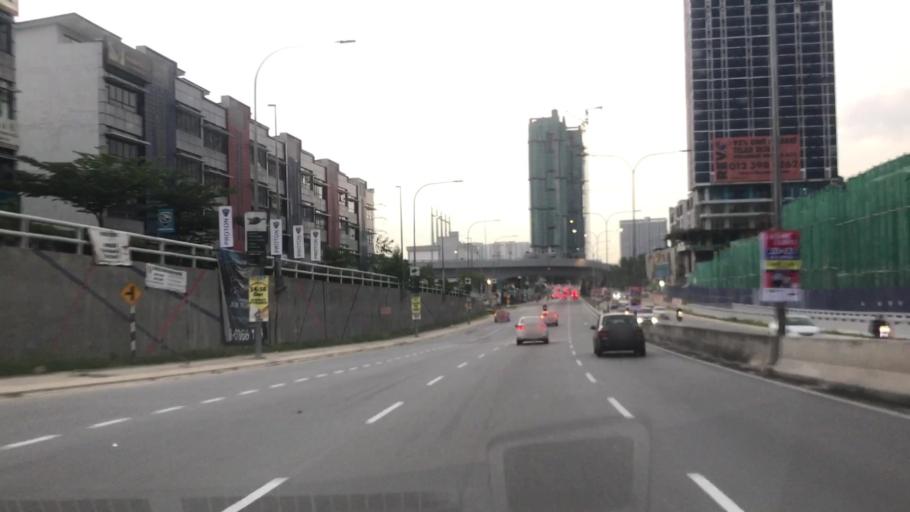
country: MY
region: Selangor
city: Kampong Baharu Balakong
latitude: 3.0502
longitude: 101.6699
